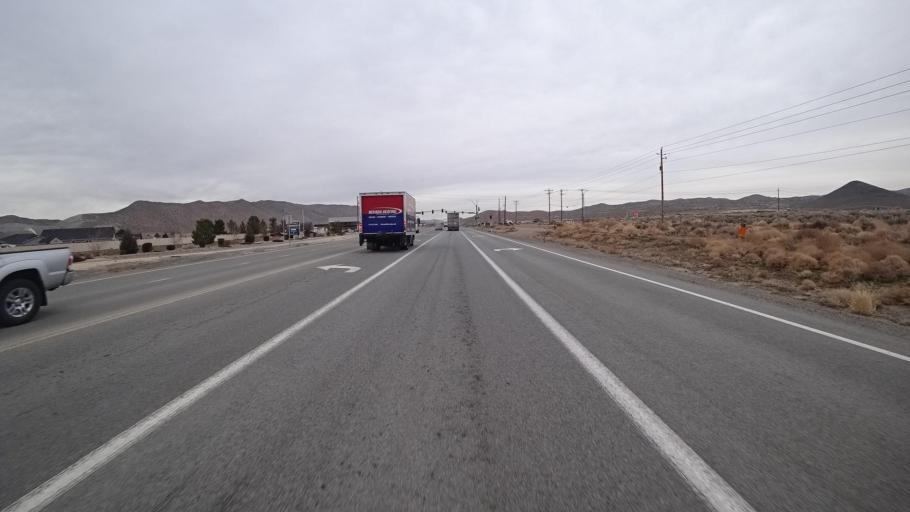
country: US
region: Nevada
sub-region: Washoe County
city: Spanish Springs
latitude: 39.6649
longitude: -119.7035
